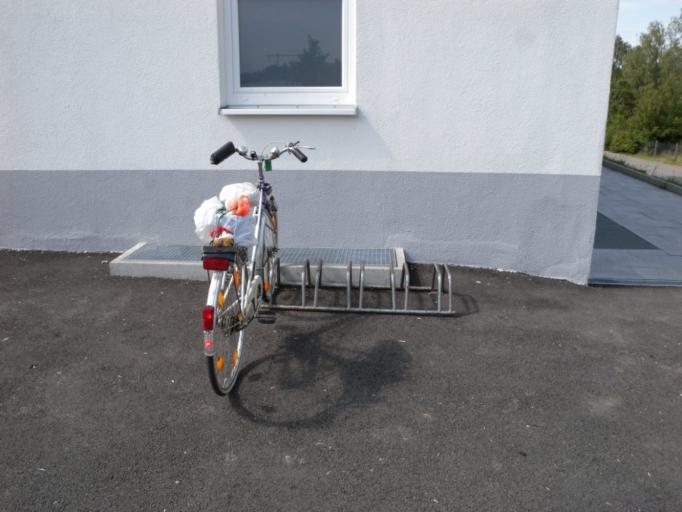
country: DE
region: Baden-Wuerttemberg
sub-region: Regierungsbezirk Stuttgart
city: Urbach
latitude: 48.8051
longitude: 9.5748
